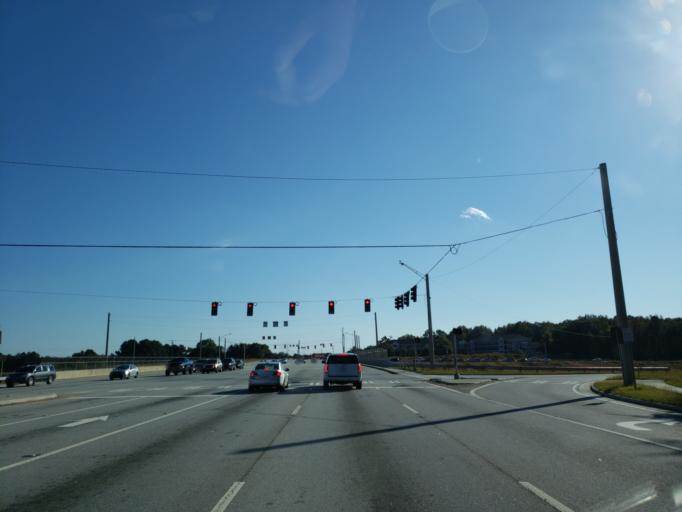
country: US
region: Georgia
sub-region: Gwinnett County
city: Lawrenceville
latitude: 33.9804
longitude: -83.9854
